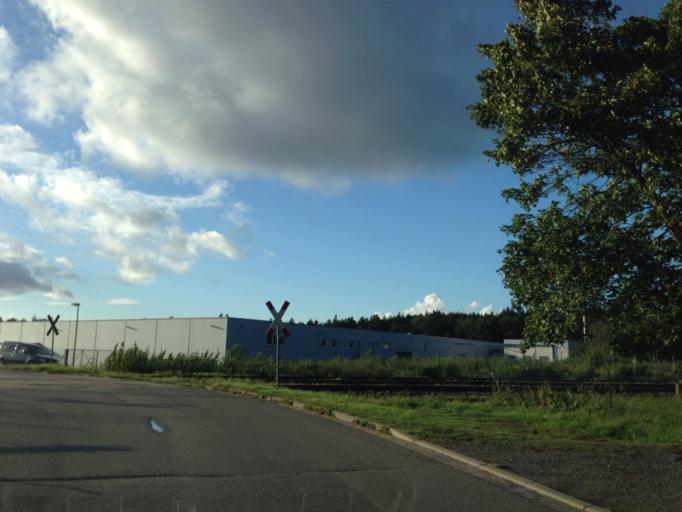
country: DE
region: Lower Saxony
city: Wendisch Evern
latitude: 53.2477
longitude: 10.4852
